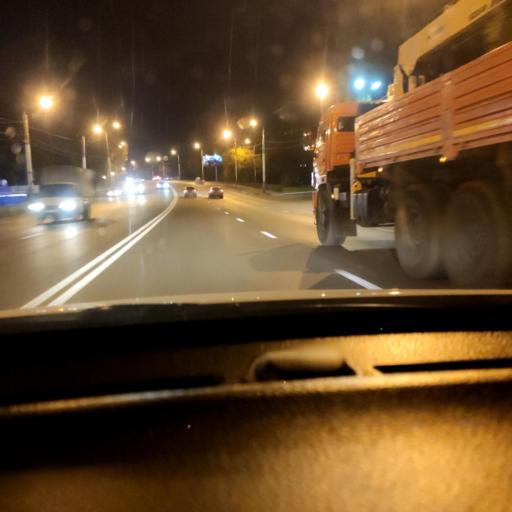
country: RU
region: Voronezj
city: Maslovka
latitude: 51.6205
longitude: 39.2361
